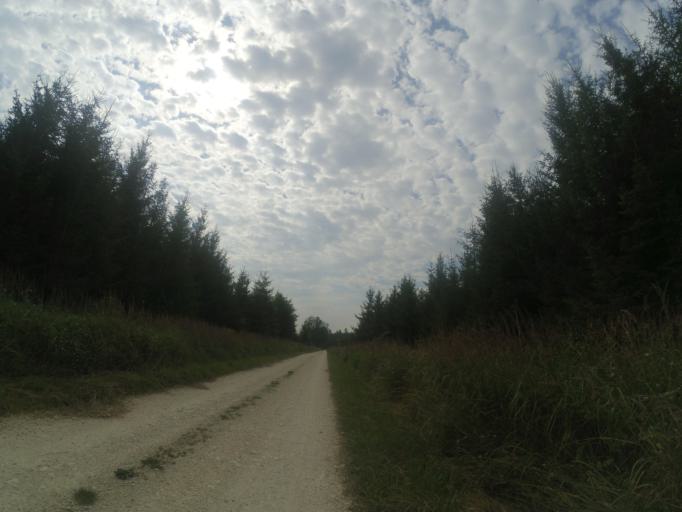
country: DE
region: Baden-Wuerttemberg
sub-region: Tuebingen Region
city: Lonsee
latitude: 48.5047
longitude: 9.8861
